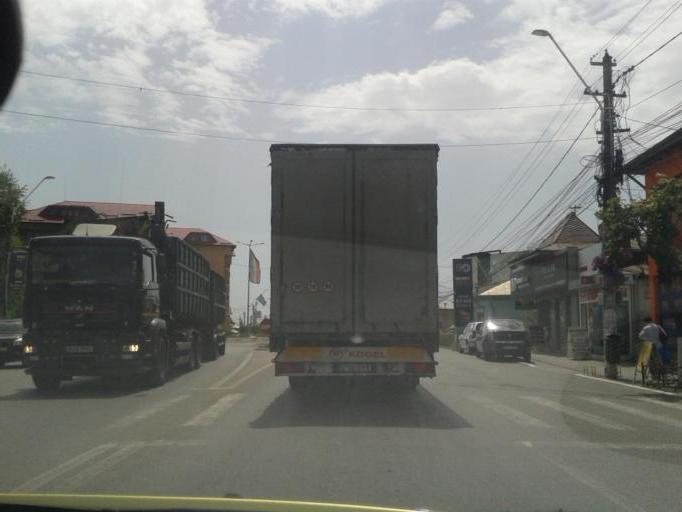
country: RO
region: Dambovita
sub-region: Oras Gaesti
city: Gaesti
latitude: 44.7189
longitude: 25.3224
